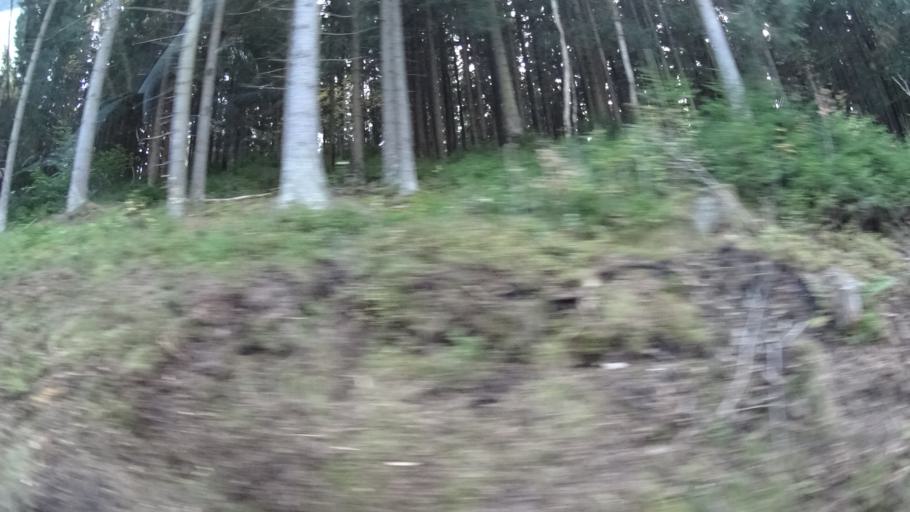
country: DE
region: Thuringia
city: Bermbach
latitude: 50.6910
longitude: 10.6360
